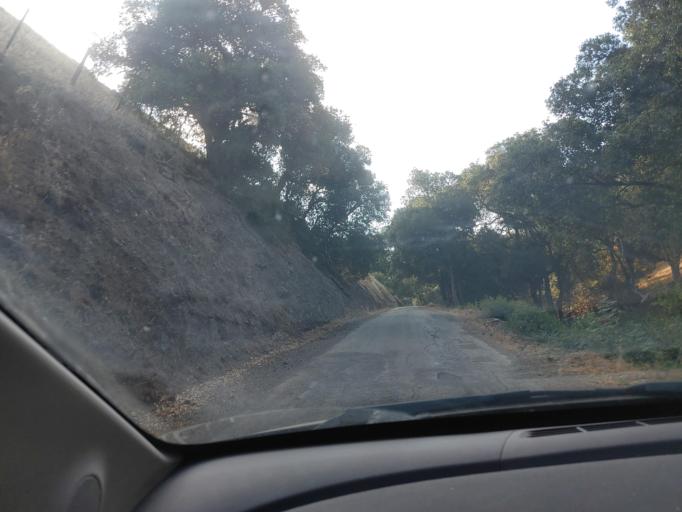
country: US
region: California
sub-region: San Benito County
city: Ridgemark
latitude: 36.7697
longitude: -121.2018
